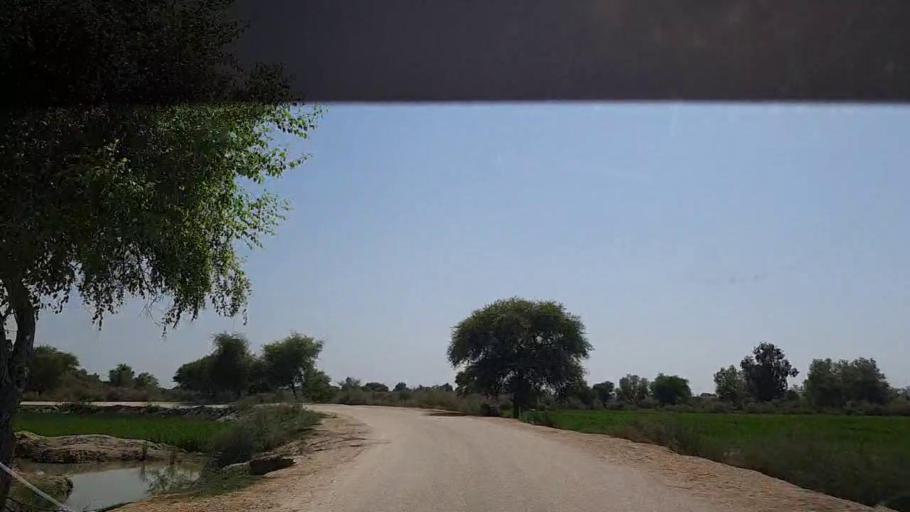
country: PK
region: Sindh
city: Ghauspur
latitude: 28.1584
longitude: 69.1598
